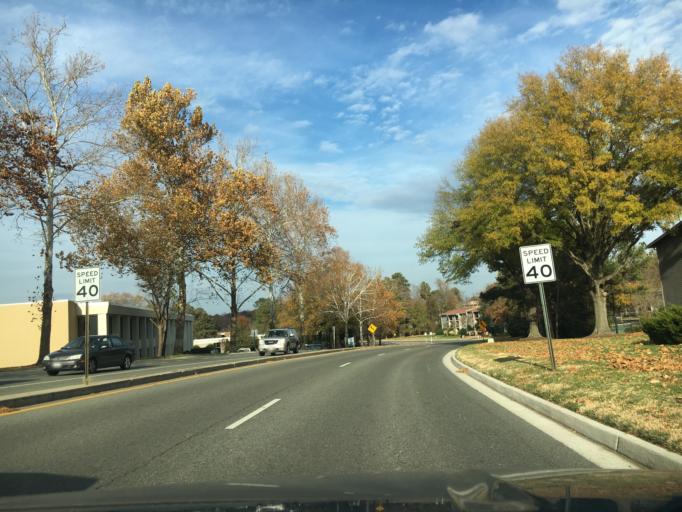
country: US
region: Virginia
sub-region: Henrico County
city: Tuckahoe
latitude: 37.5997
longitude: -77.5457
